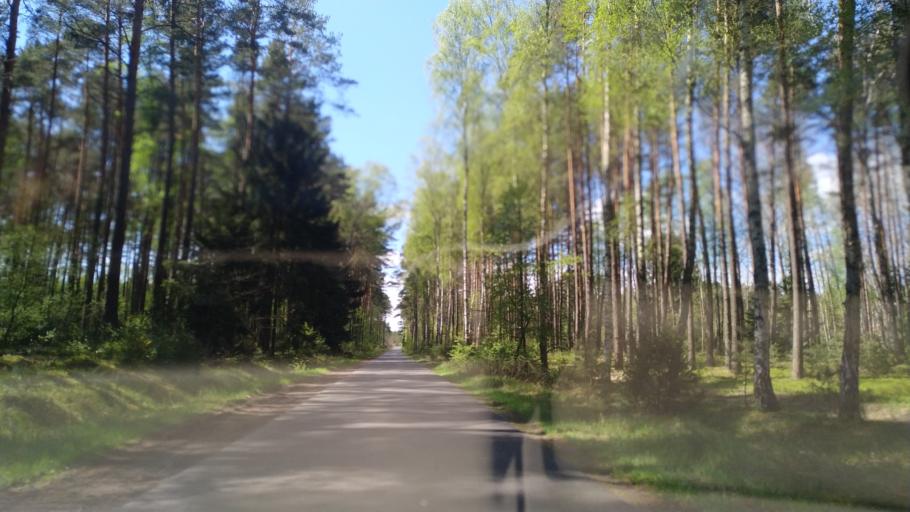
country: PL
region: Greater Poland Voivodeship
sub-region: Powiat zlotowski
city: Tarnowka
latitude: 53.2706
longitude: 16.8714
